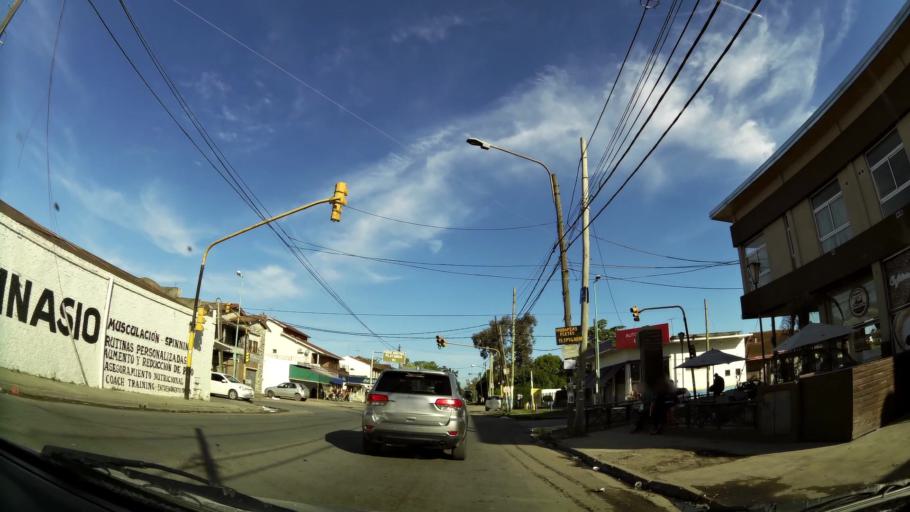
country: AR
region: Buenos Aires
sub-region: Partido de Quilmes
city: Quilmes
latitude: -34.8095
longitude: -58.2101
